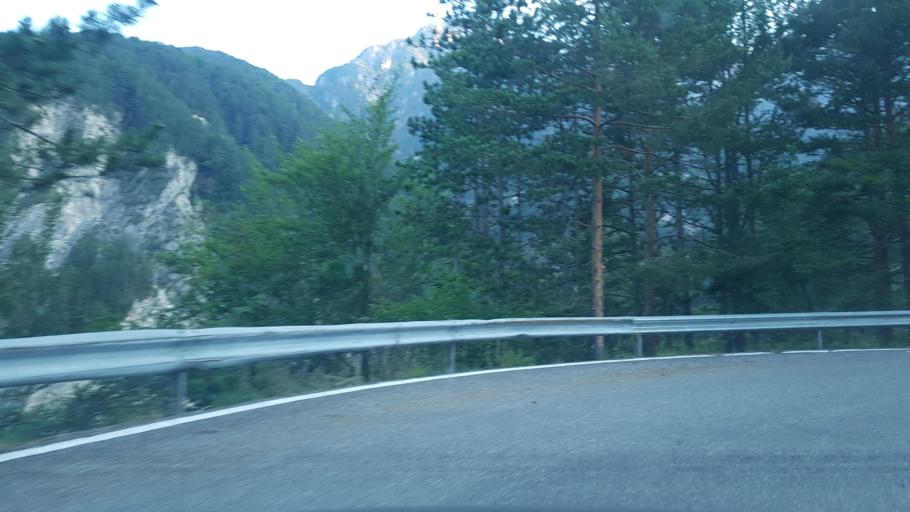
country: IT
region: Friuli Venezia Giulia
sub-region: Provincia di Udine
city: Dogna
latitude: 46.4518
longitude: 13.3568
